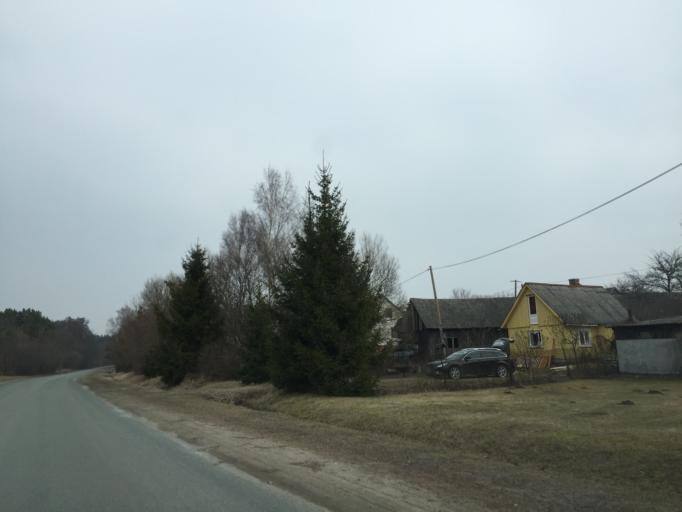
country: LV
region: Salacgrivas
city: Ainazi
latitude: 58.0135
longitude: 24.4499
